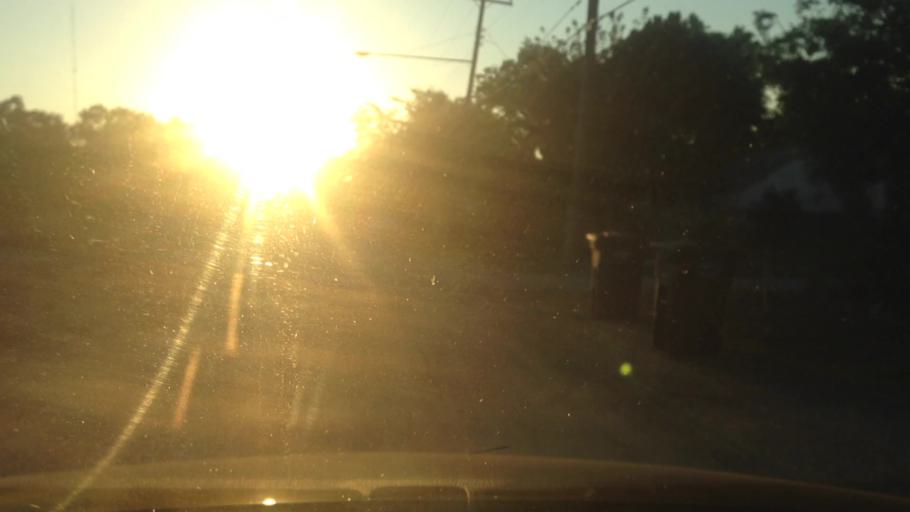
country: US
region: Texas
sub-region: Tarrant County
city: Haltom City
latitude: 32.7969
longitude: -97.3028
